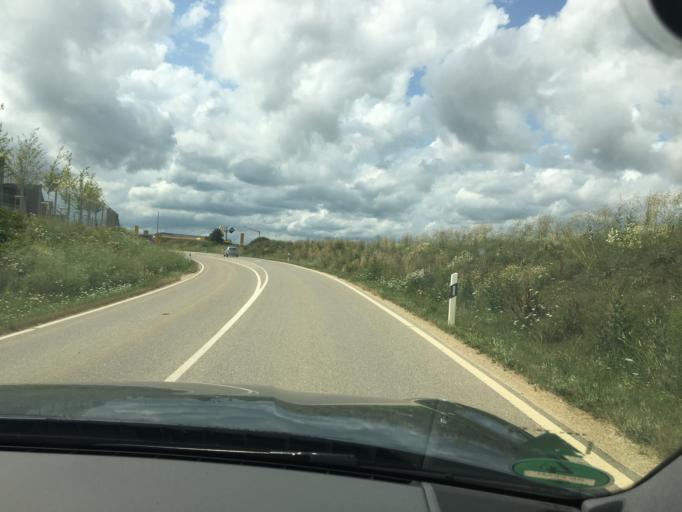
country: DE
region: Baden-Wuerttemberg
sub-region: Tuebingen Region
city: Merklingen
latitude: 48.5164
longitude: 9.7642
